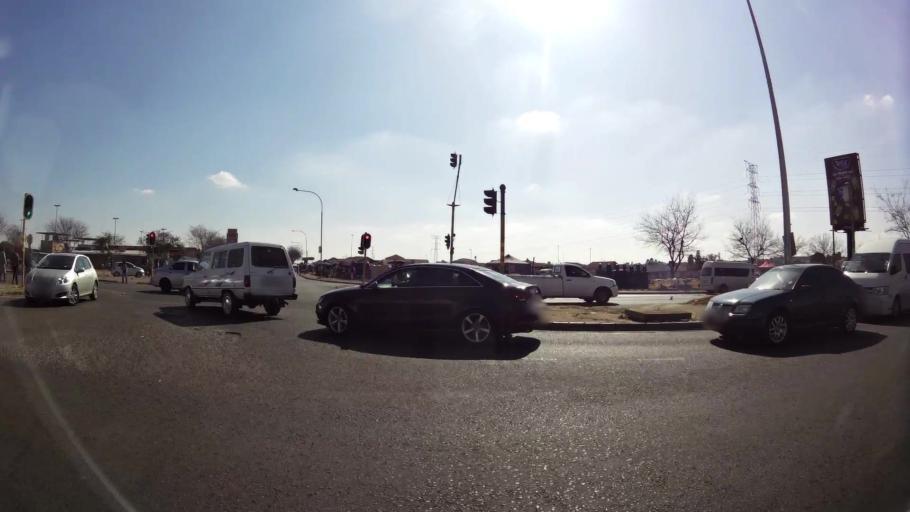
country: ZA
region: Gauteng
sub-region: City of Johannesburg Metropolitan Municipality
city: Soweto
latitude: -26.2866
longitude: 27.8508
